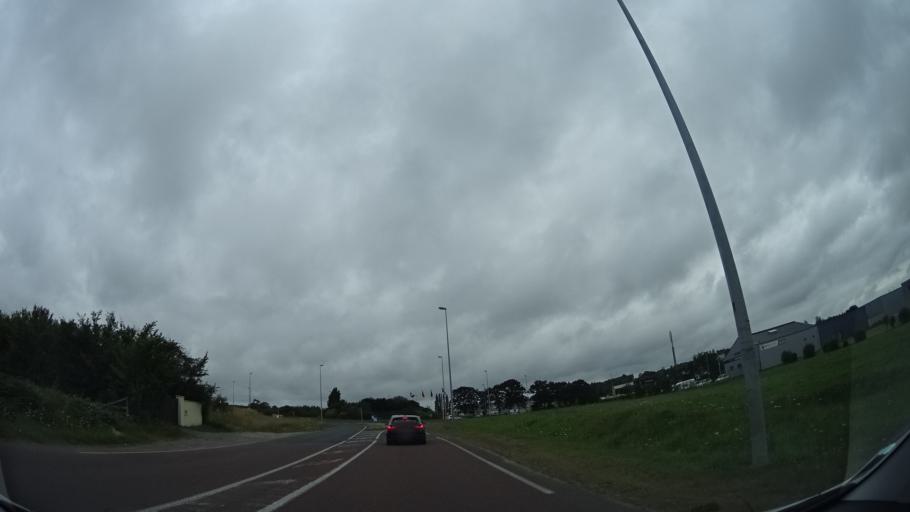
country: FR
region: Lower Normandy
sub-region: Departement de la Manche
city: La Haye-du-Puits
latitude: 49.2776
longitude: -1.5407
